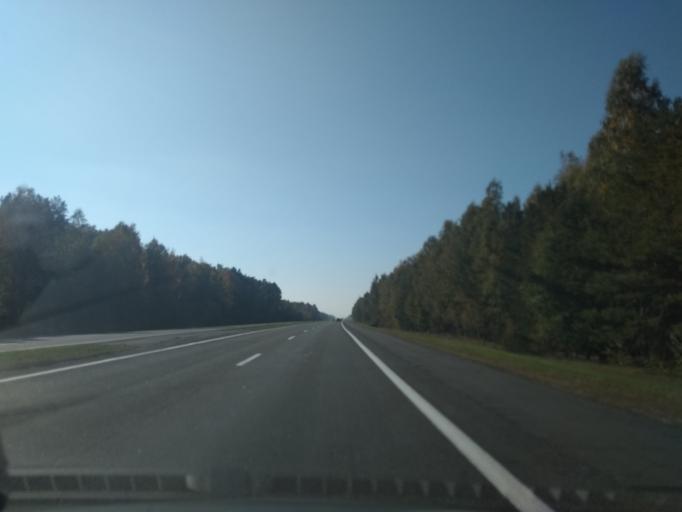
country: BY
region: Brest
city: Ivatsevichy
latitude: 52.7689
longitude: 25.5350
